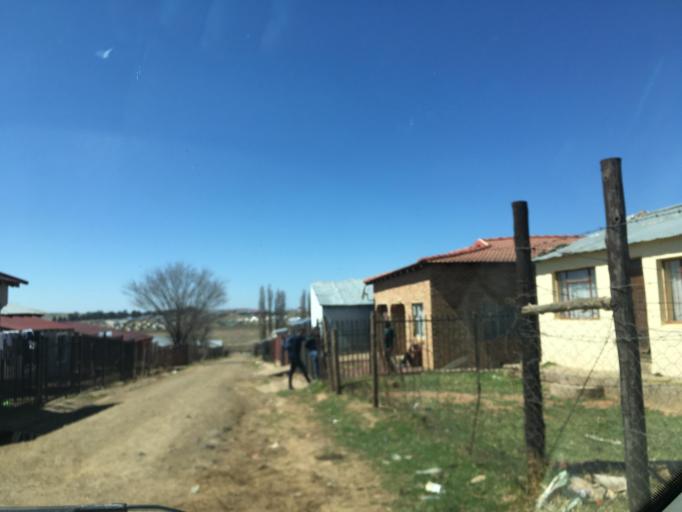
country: ZA
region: Eastern Cape
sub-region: Chris Hani District Municipality
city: Elliot
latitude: -31.3303
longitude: 27.8243
